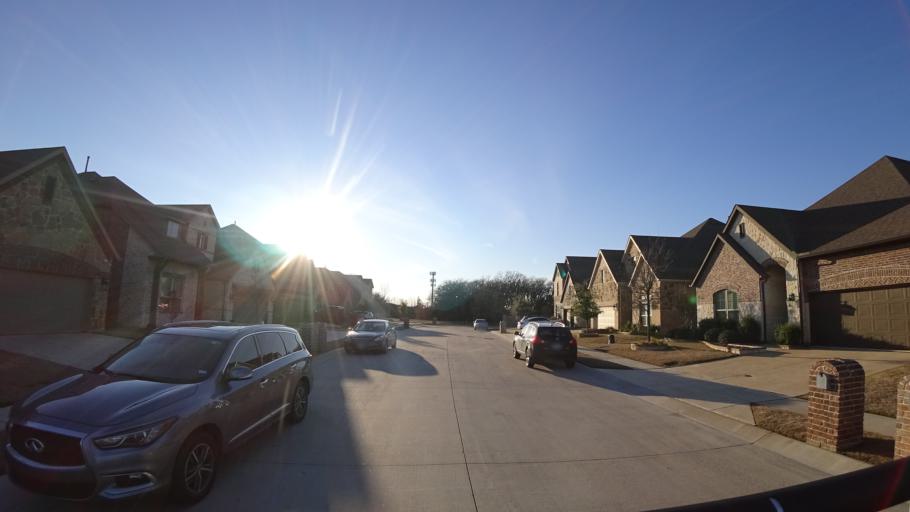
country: US
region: Texas
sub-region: Dallas County
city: Coppell
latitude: 32.9938
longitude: -96.9991
